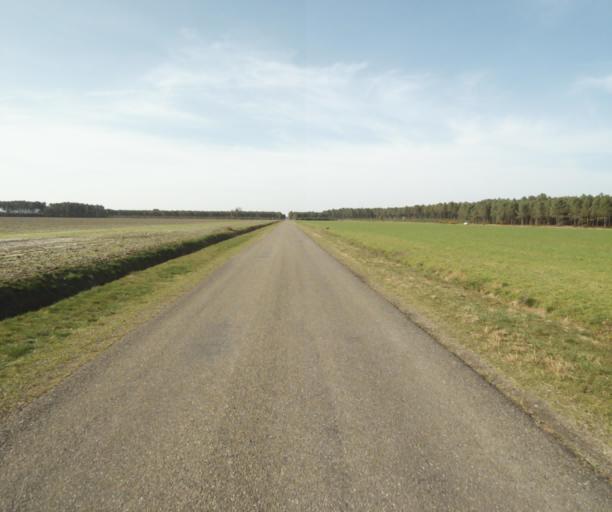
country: FR
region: Aquitaine
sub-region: Departement des Landes
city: Roquefort
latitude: 44.1786
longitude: -0.2049
